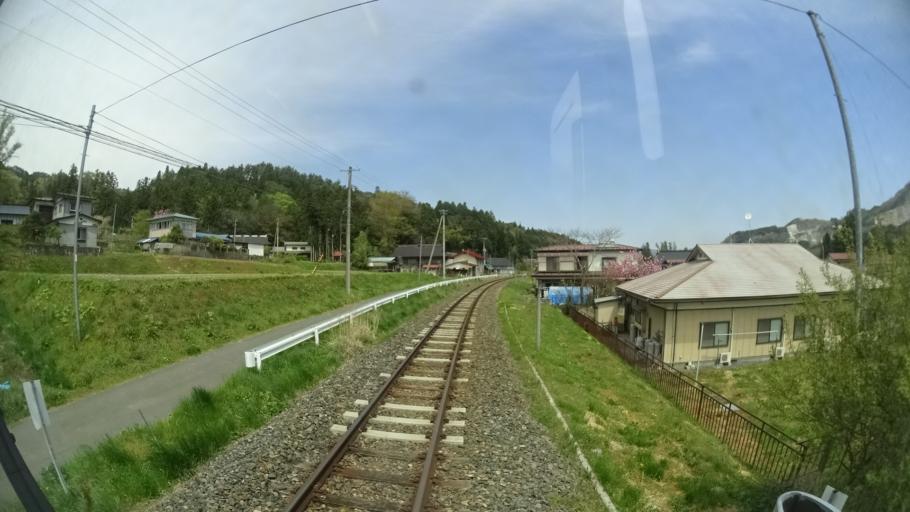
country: JP
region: Iwate
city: Ichinoseki
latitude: 38.9634
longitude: 141.2400
